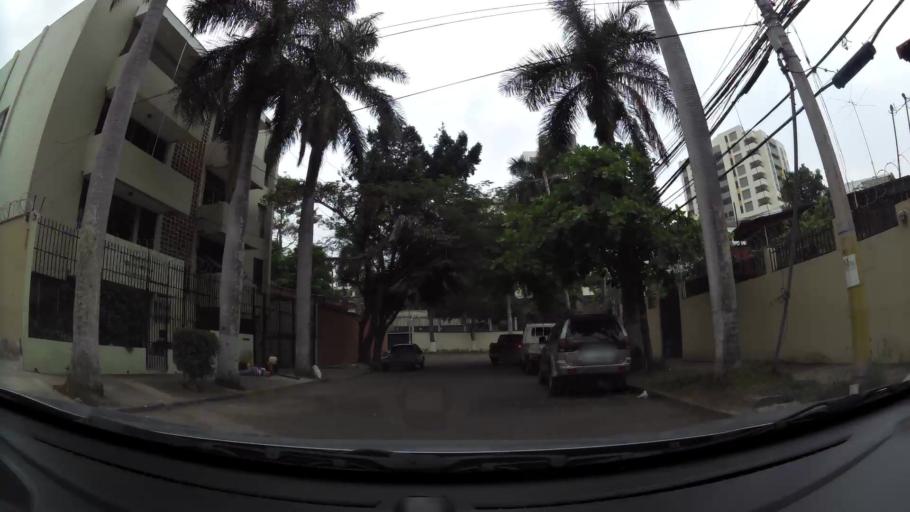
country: HN
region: Francisco Morazan
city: Tegucigalpa
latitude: 14.1030
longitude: -87.1952
